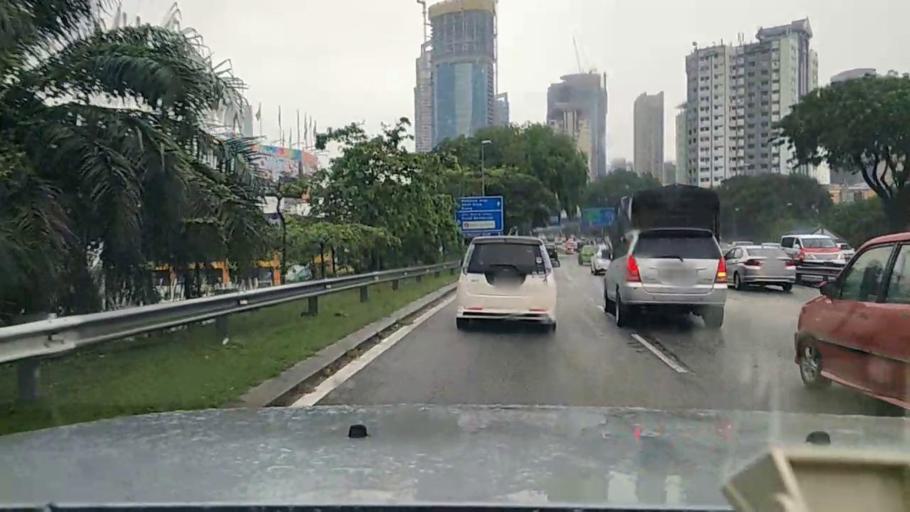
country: MY
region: Kuala Lumpur
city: Kuala Lumpur
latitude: 3.1132
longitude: 101.6812
